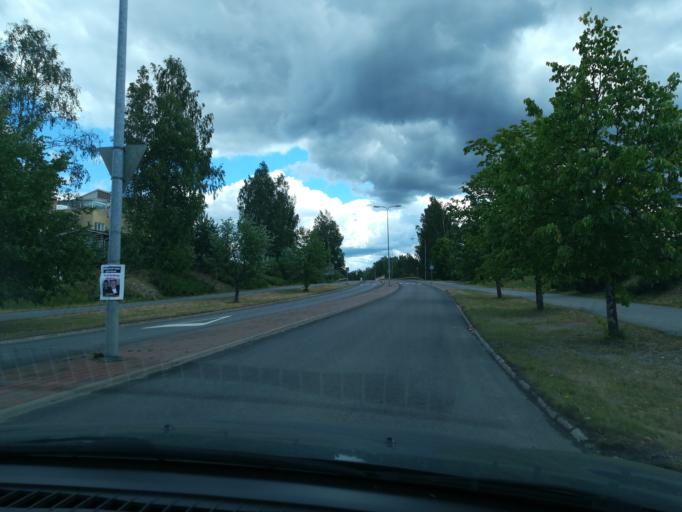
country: FI
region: Southern Savonia
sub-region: Mikkeli
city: Maentyharju
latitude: 61.4176
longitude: 26.8809
